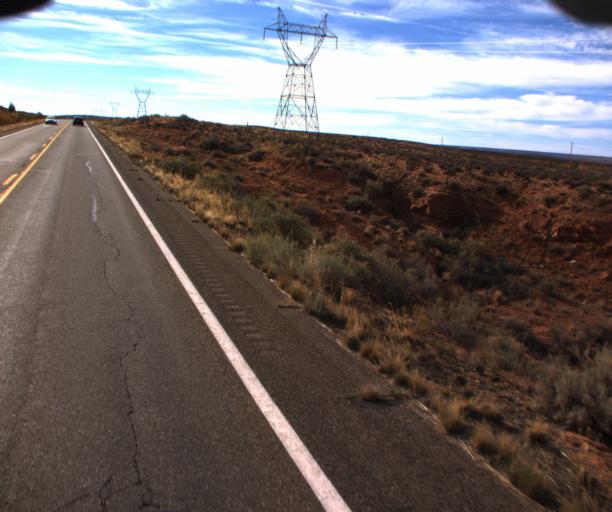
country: US
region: Arizona
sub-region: Coconino County
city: LeChee
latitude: 36.8501
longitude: -111.3330
